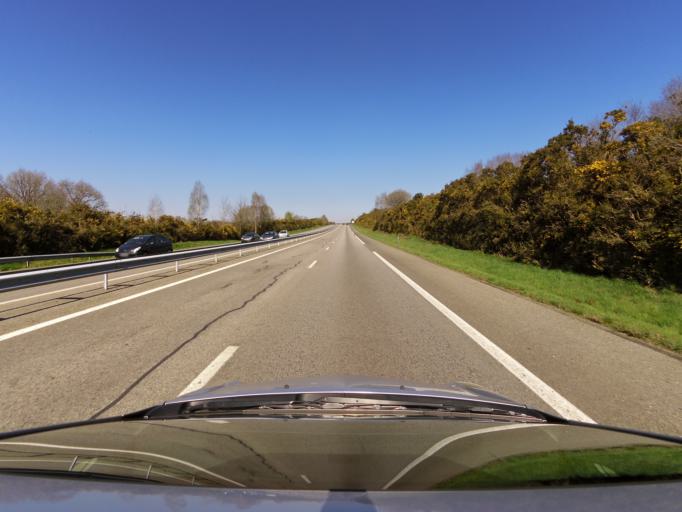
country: FR
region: Brittany
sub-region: Departement du Morbihan
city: Augan
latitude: 47.9328
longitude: -2.2499
